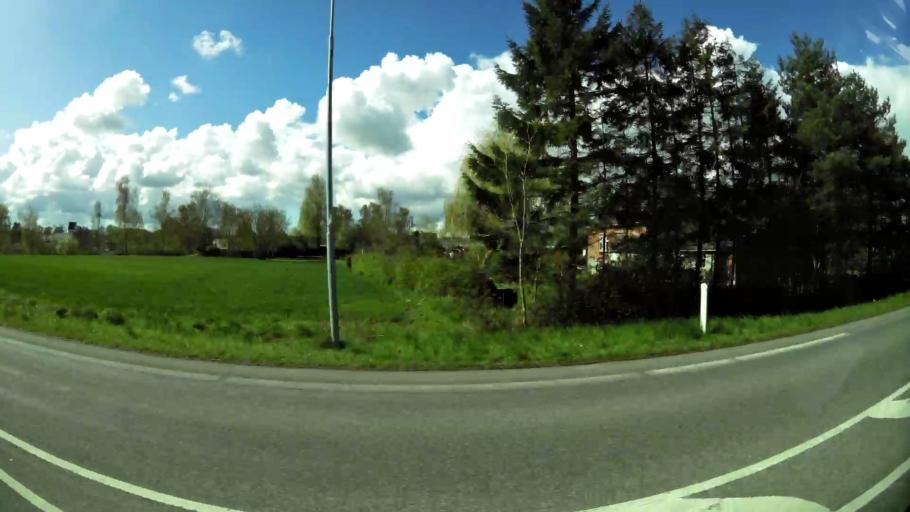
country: DK
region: South Denmark
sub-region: Middelfart Kommune
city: Brenderup
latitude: 55.4839
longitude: 9.9799
